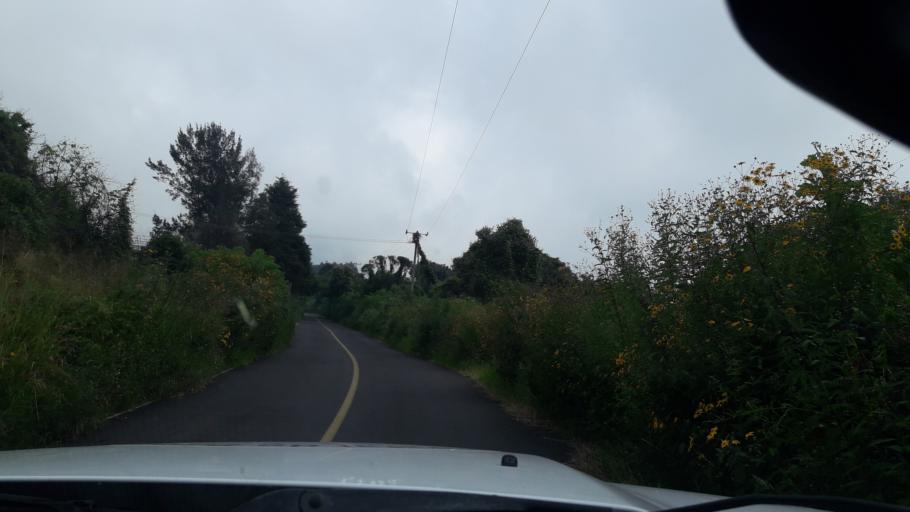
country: MX
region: Colima
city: Suchitlan
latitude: 19.4128
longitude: -103.6479
